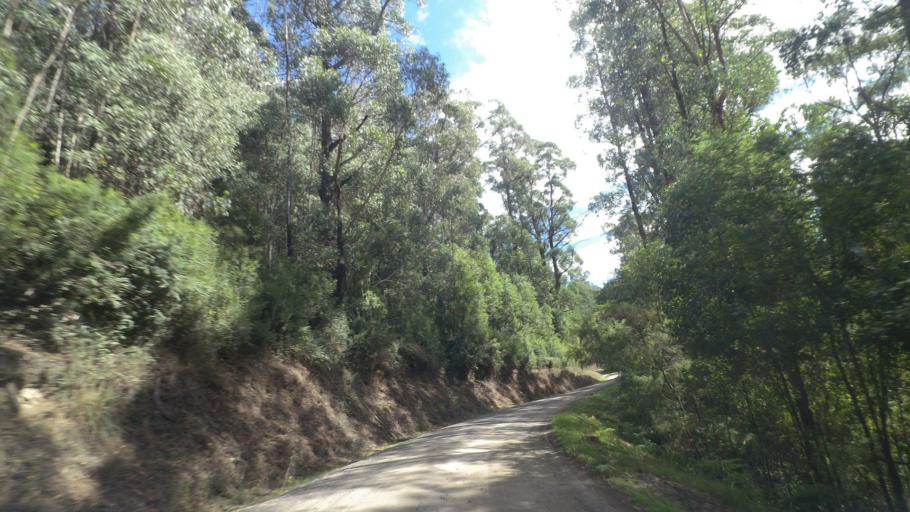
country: AU
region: Victoria
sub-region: Cardinia
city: Bunyip
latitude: -37.9457
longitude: 145.8048
